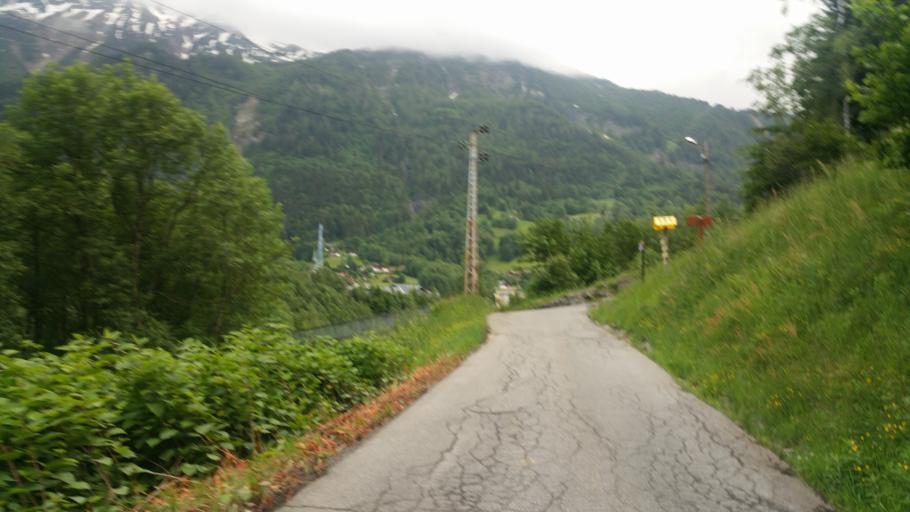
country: FR
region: Rhone-Alpes
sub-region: Departement de la Haute-Savoie
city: Les Houches
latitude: 45.8951
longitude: 6.7990
